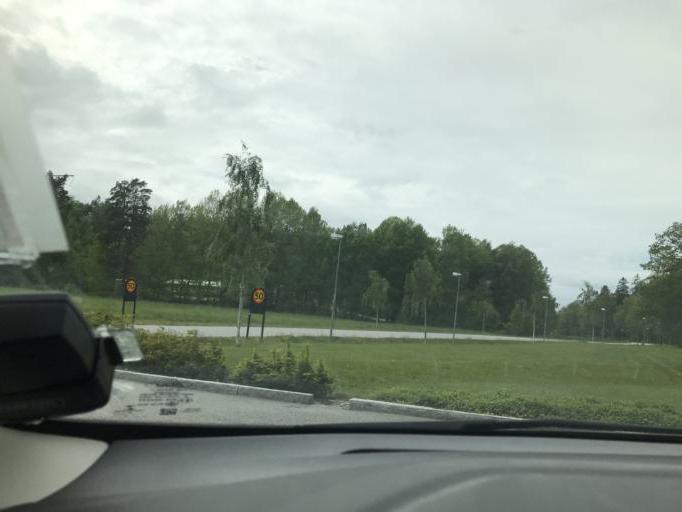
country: SE
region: Stockholm
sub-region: Botkyrka Kommun
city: Alby
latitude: 59.2186
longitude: 17.8470
